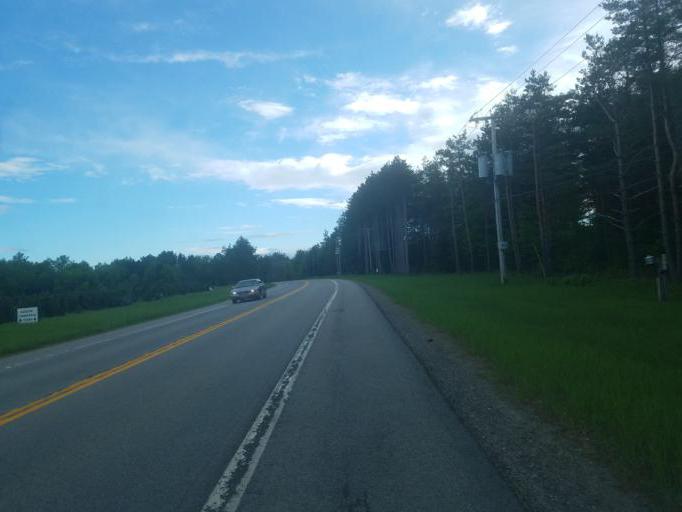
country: US
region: New York
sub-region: Herkimer County
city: Herkimer
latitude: 43.3090
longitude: -74.9703
